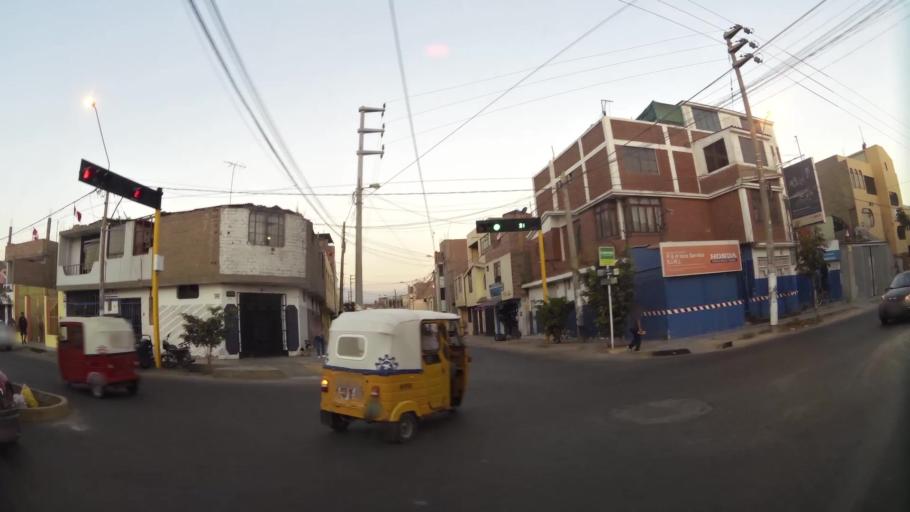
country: PE
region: Ica
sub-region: Provincia de Ica
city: Ica
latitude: -14.0674
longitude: -75.7328
